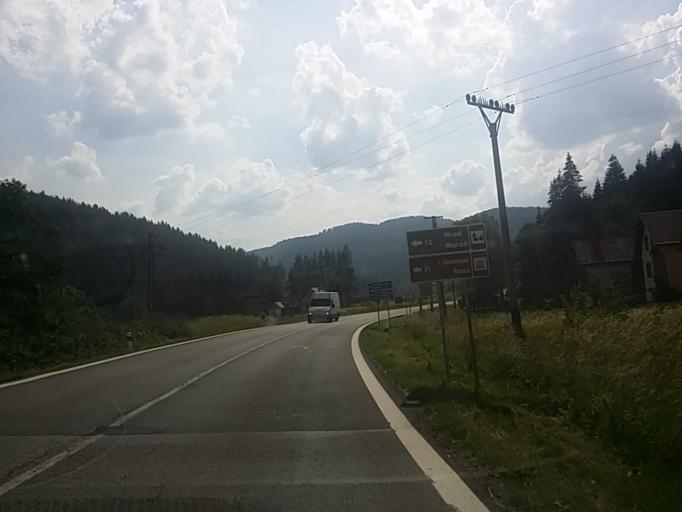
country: SK
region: Banskobystricky
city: Revuca
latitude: 48.8201
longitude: 20.1445
